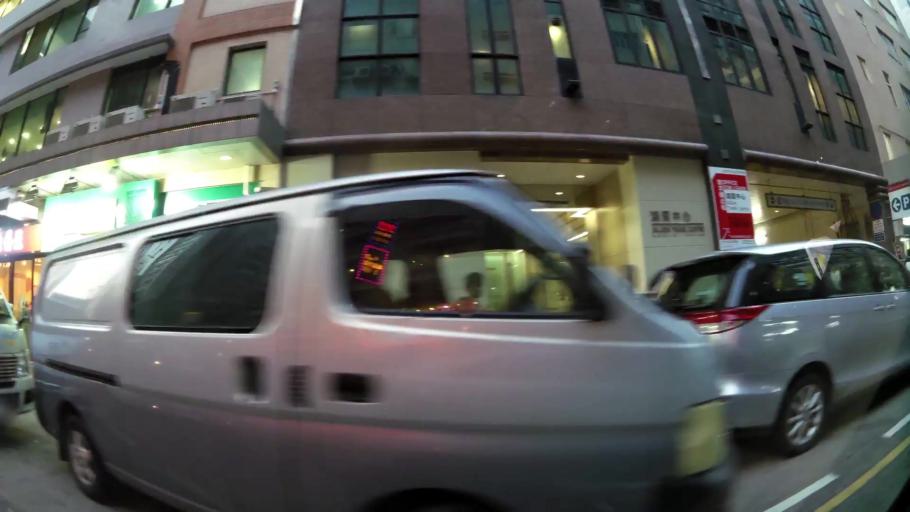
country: HK
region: Kowloon City
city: Kowloon
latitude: 22.3124
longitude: 114.2200
